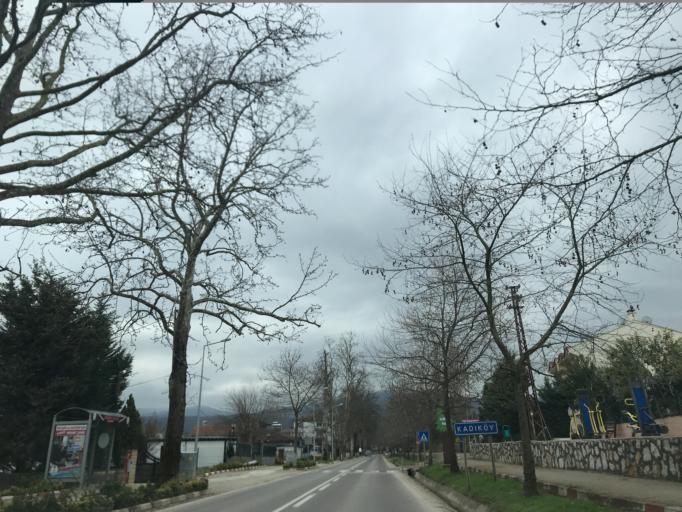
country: TR
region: Yalova
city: Kadikoy
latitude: 40.6225
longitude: 29.2196
